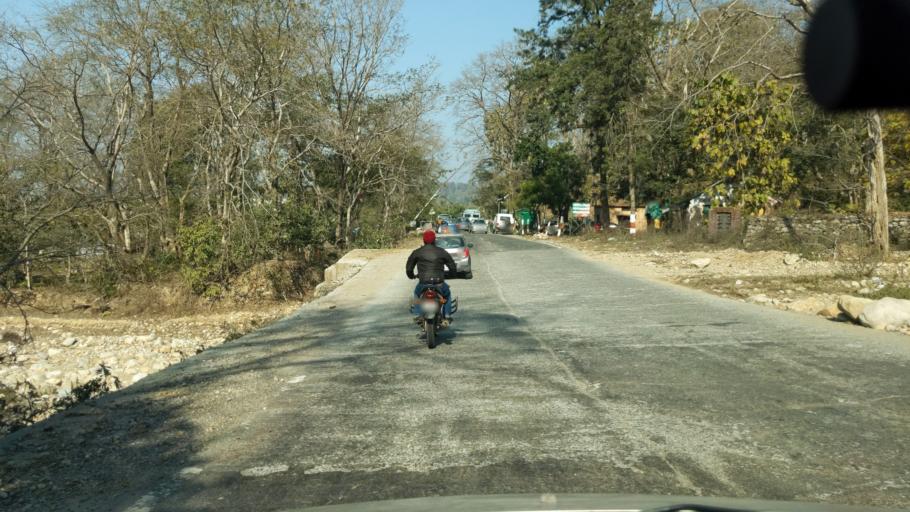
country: IN
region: Uttarakhand
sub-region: Naini Tal
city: Ramnagar
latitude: 29.3855
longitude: 79.1424
